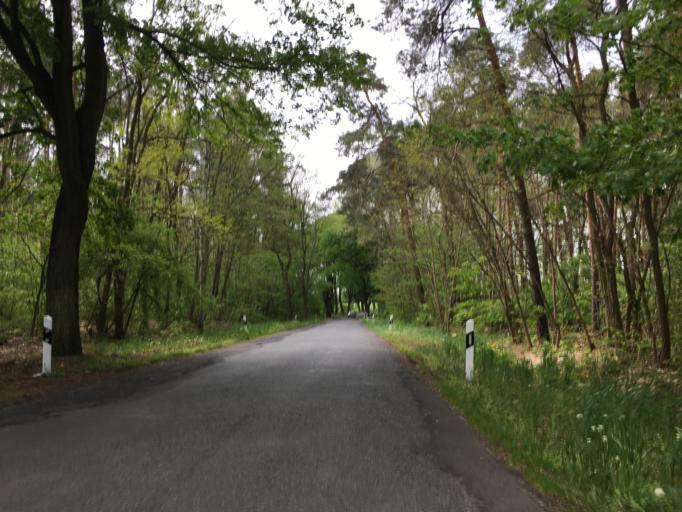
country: DE
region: Brandenburg
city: Rudnitz
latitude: 52.7303
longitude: 13.6474
